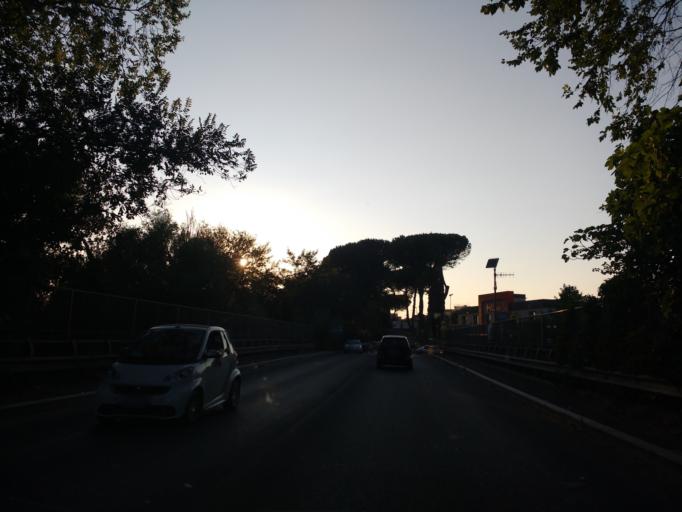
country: IT
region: Latium
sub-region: Citta metropolitana di Roma Capitale
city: Villa Adriana
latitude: 41.9557
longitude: 12.7633
